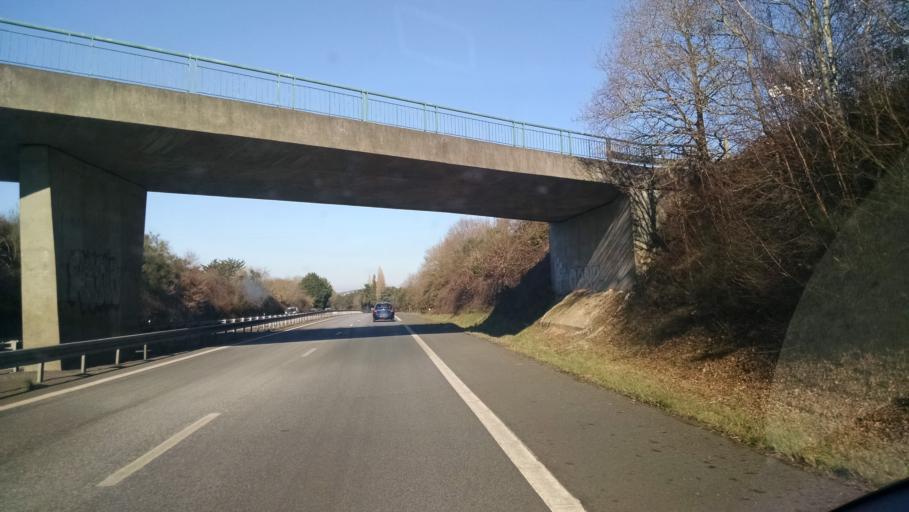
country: FR
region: Brittany
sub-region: Departement du Morbihan
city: Landevant
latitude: 47.7478
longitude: -3.1045
